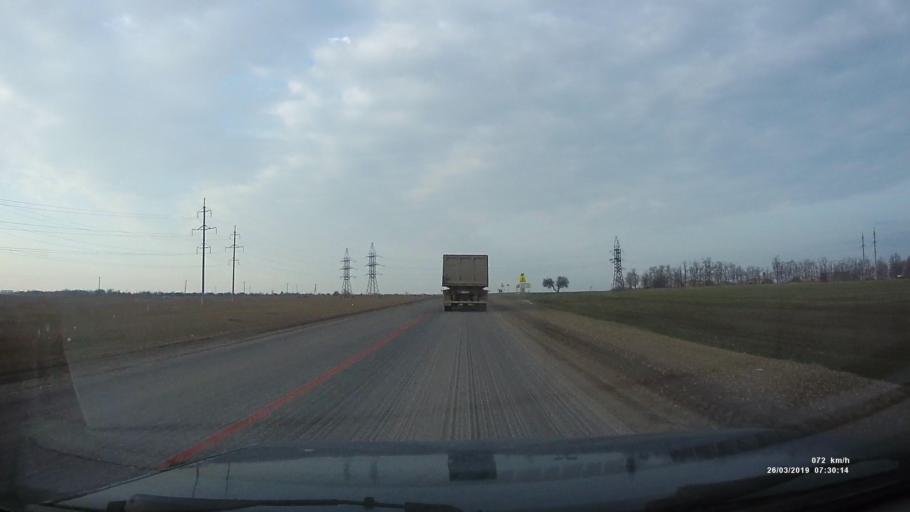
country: RU
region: Rostov
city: Novobessergenovka
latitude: 47.2381
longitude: 38.8090
